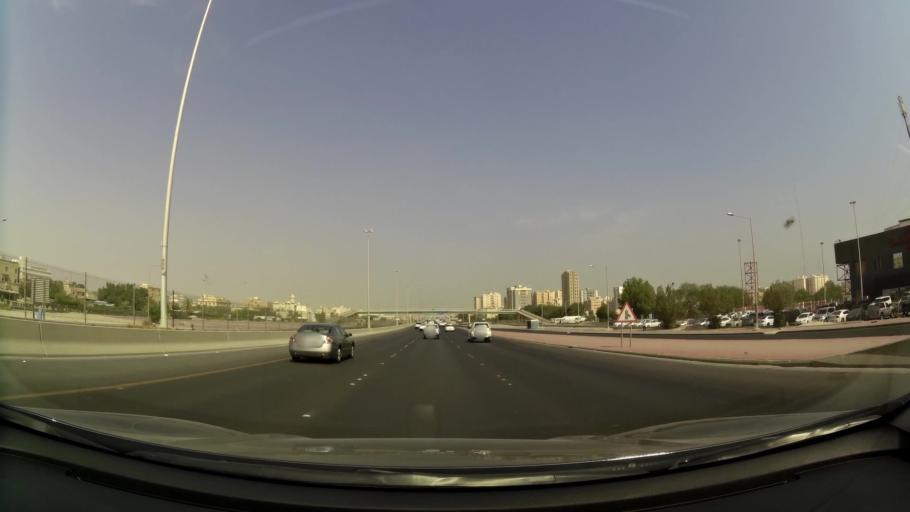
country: KW
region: Al Ahmadi
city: Al Manqaf
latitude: 29.0951
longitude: 48.1166
